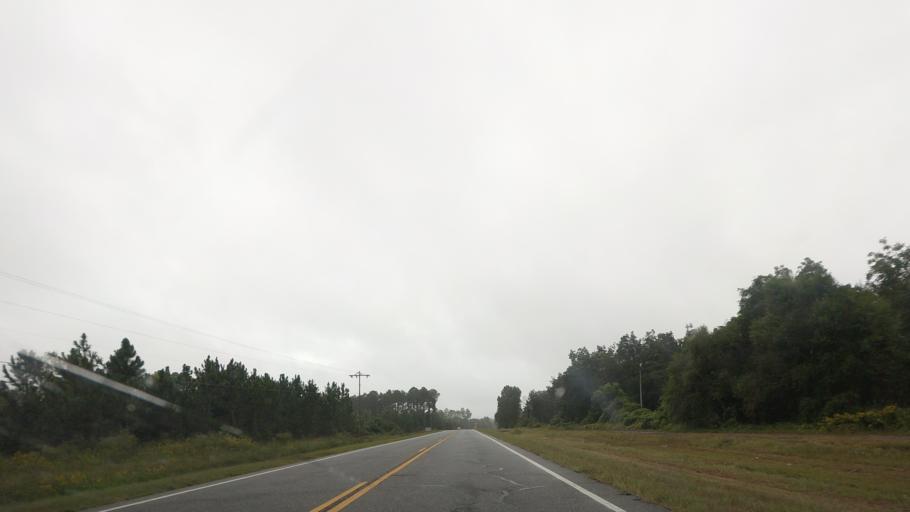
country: US
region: Georgia
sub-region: Ben Hill County
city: Fitzgerald
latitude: 31.7640
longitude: -83.2454
